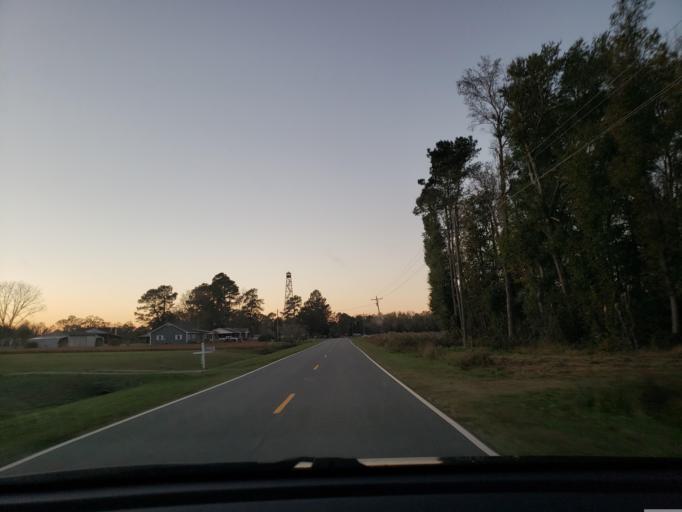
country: US
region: North Carolina
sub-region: Duplin County
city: Beulaville
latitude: 34.7904
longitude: -77.7623
